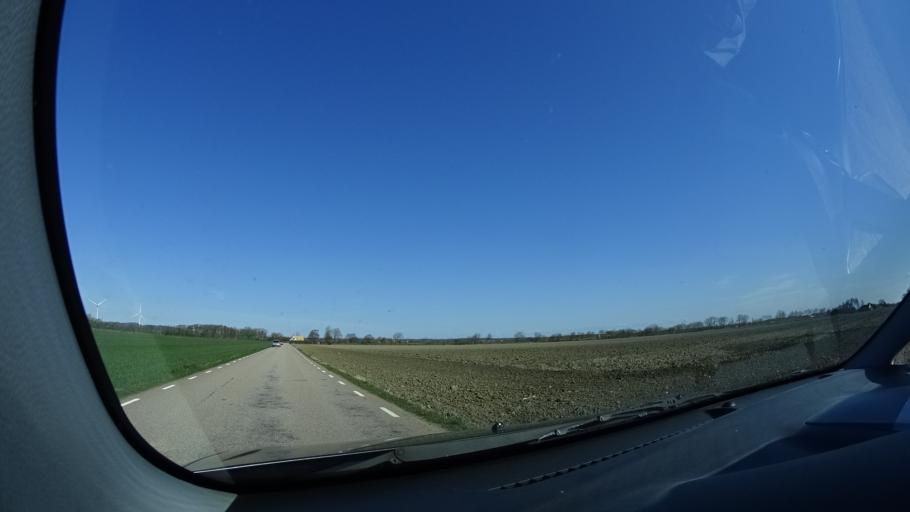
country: SE
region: Skane
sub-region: Hoganas Kommun
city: Hoganas
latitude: 56.2165
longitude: 12.5935
